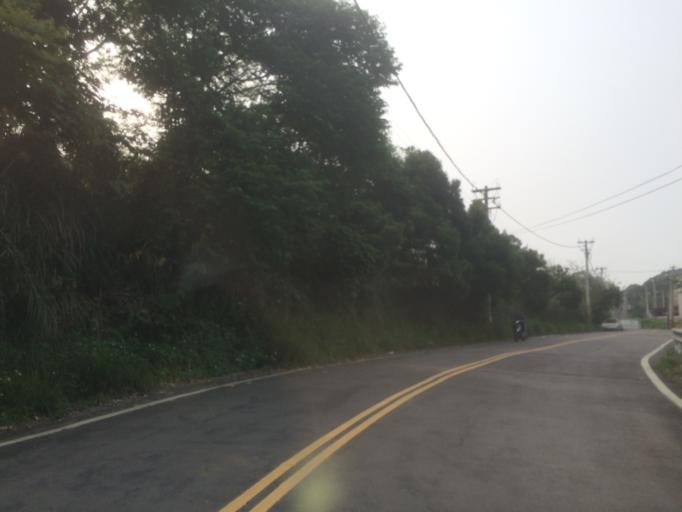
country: TW
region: Taiwan
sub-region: Hsinchu
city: Hsinchu
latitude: 24.7637
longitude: 120.9765
